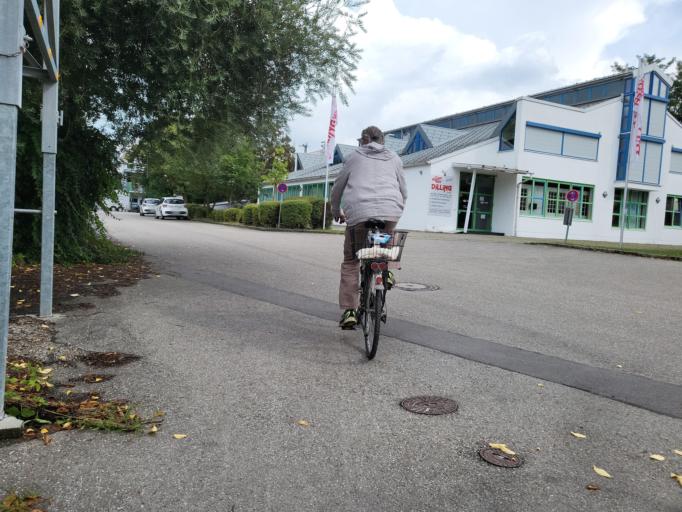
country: DE
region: Bavaria
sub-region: Upper Bavaria
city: Olching
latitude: 48.2115
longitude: 11.3323
